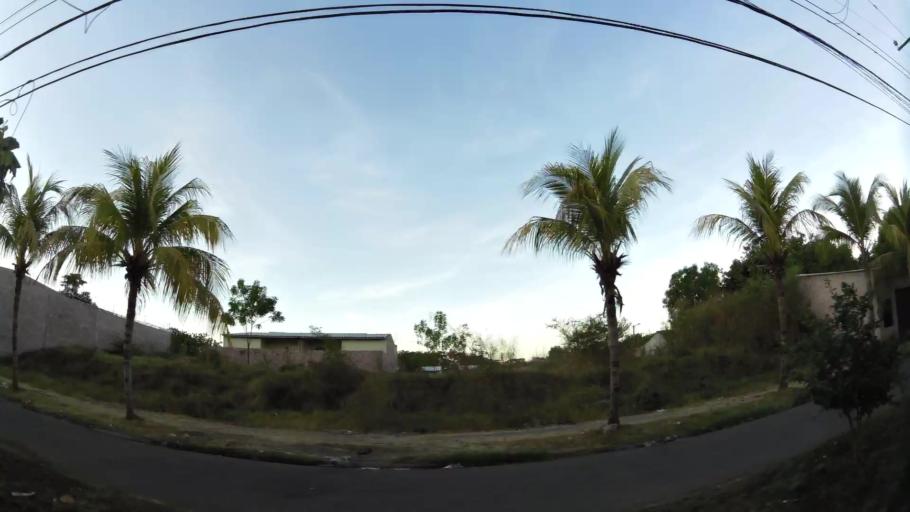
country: SV
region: San Miguel
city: San Miguel
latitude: 13.4789
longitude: -88.1584
